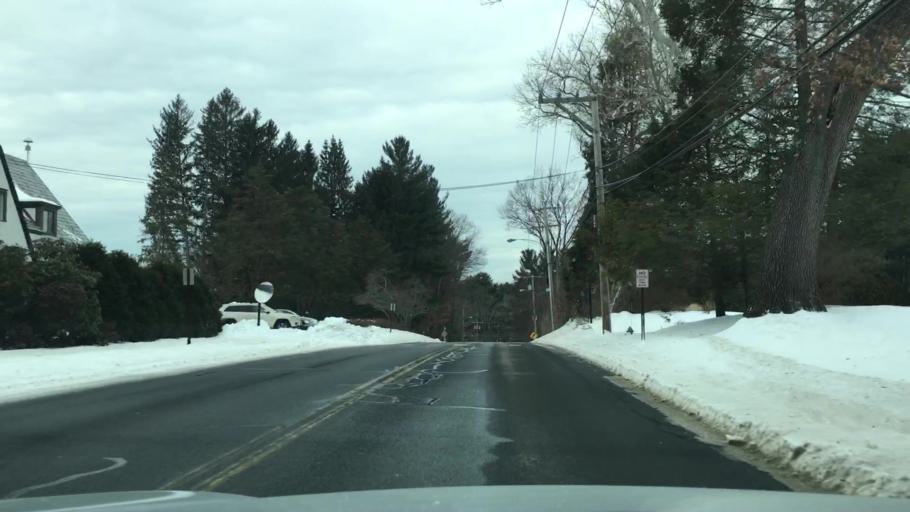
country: US
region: Massachusetts
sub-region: Hampden County
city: Longmeadow
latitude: 42.0405
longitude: -72.5695
